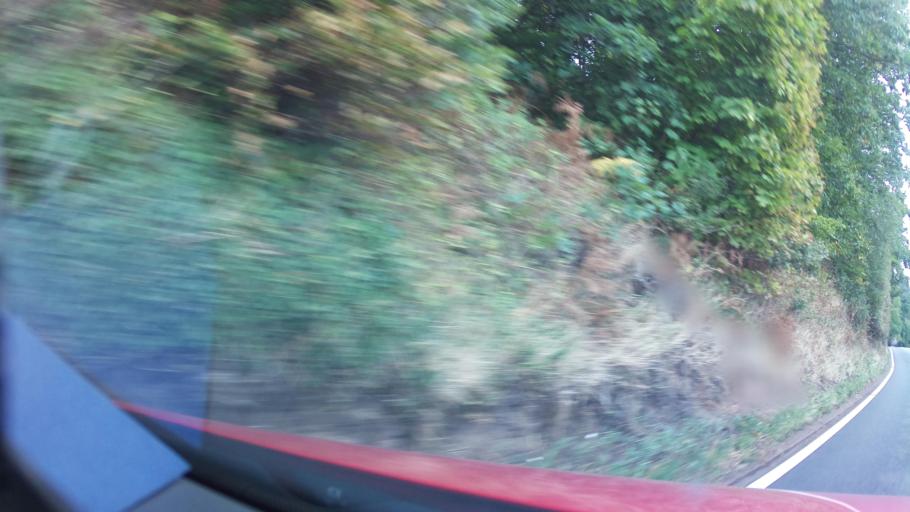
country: GB
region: England
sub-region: Shropshire
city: Bridgnorth
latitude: 52.5519
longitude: -2.4061
